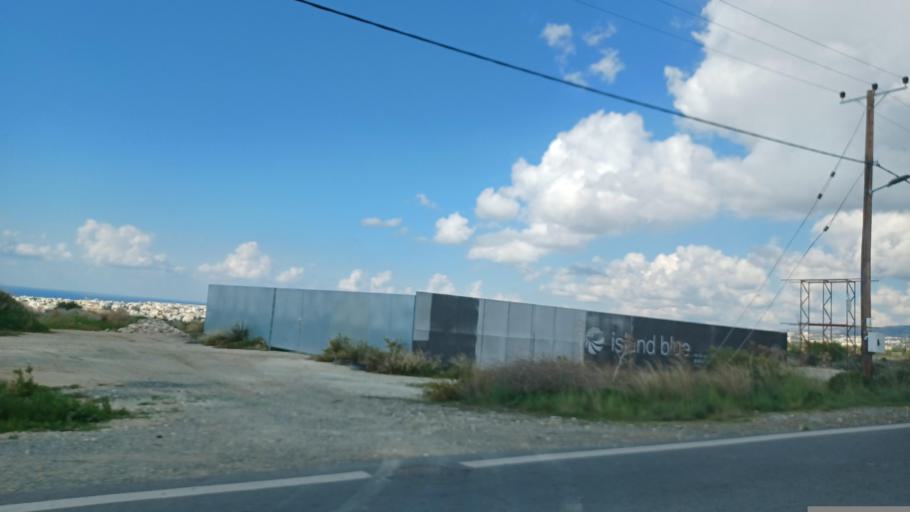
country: CY
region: Pafos
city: Paphos
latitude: 34.7724
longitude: 32.4580
